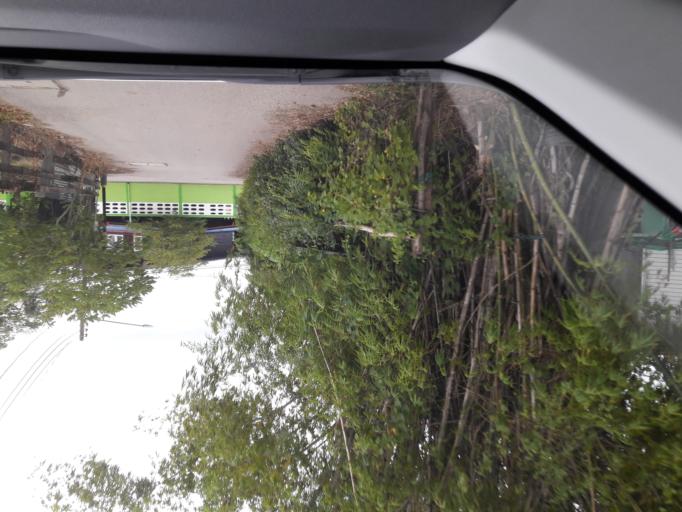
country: TH
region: Ratchaburi
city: Ratchaburi
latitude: 13.5352
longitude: 99.7910
